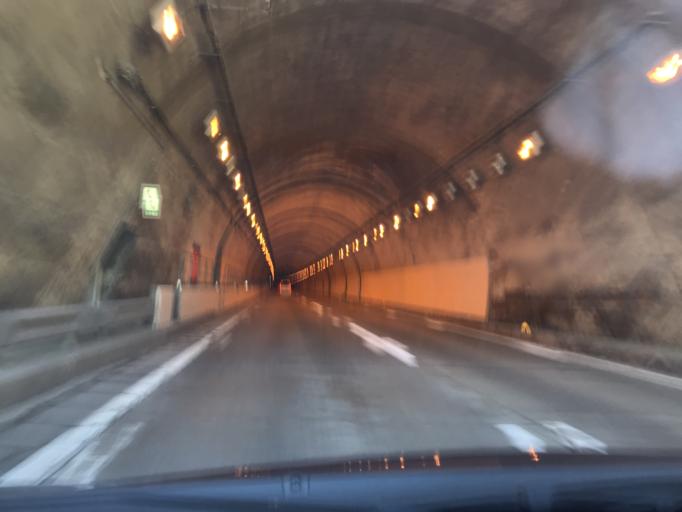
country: JP
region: Hokkaido
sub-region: Asahikawa-shi
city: Asahikawa
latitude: 43.7922
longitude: 142.2642
